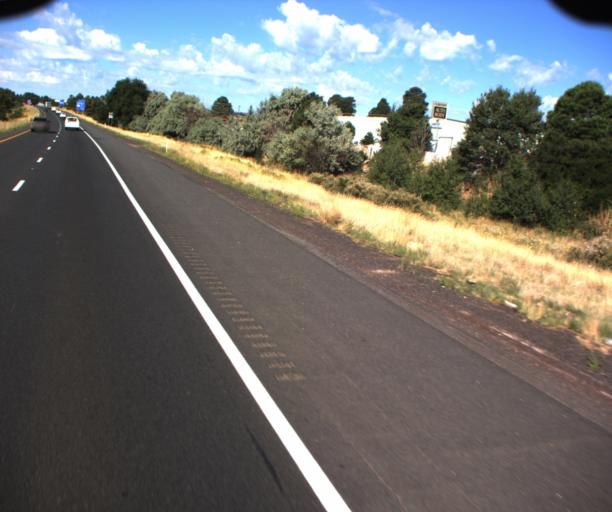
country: US
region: Arizona
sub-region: Coconino County
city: Flagstaff
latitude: 35.2129
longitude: -111.5929
